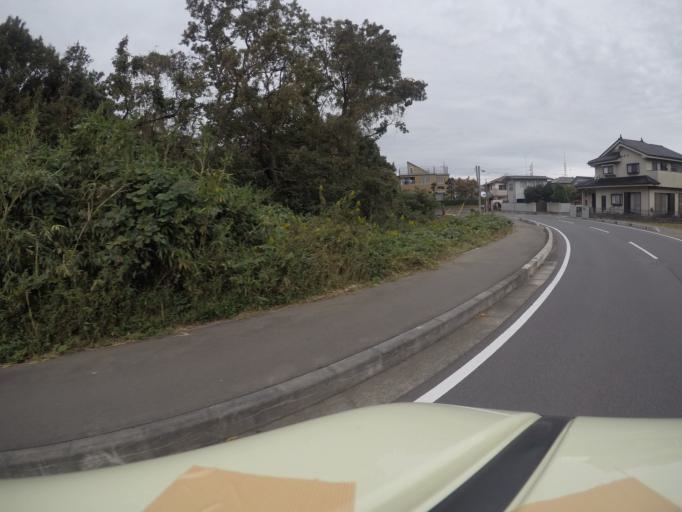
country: JP
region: Ibaraki
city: Naka
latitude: 36.0660
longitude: 140.1727
